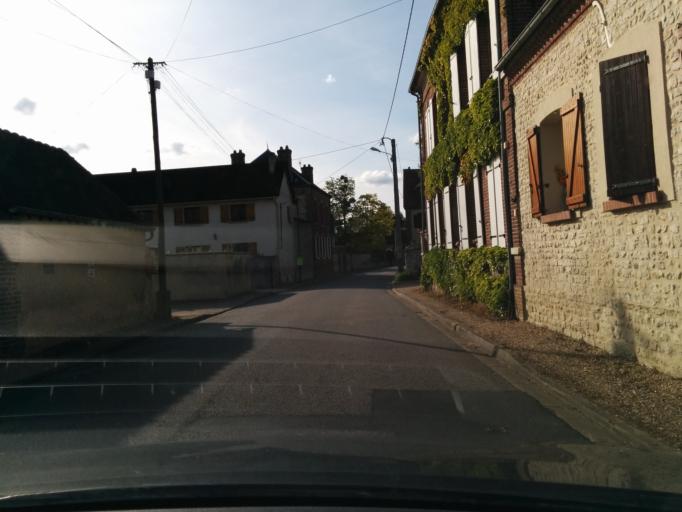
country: FR
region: Haute-Normandie
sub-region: Departement de l'Eure
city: Courcelles-sur-Seine
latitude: 49.1642
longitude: 1.4137
